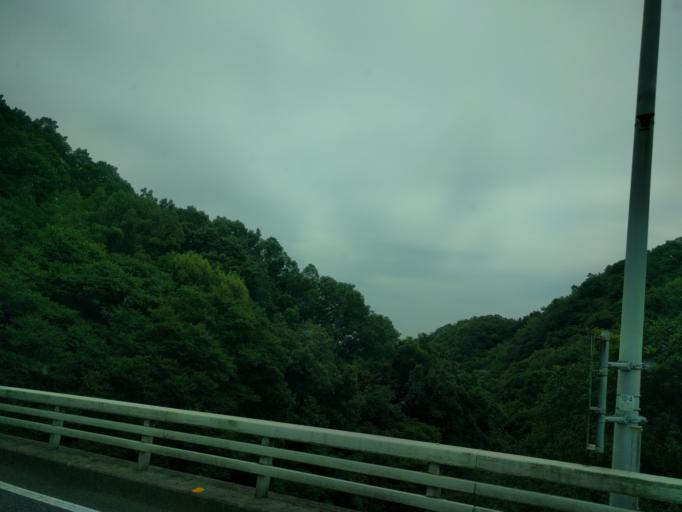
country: JP
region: Hyogo
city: Kobe
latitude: 34.6966
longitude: 135.1548
